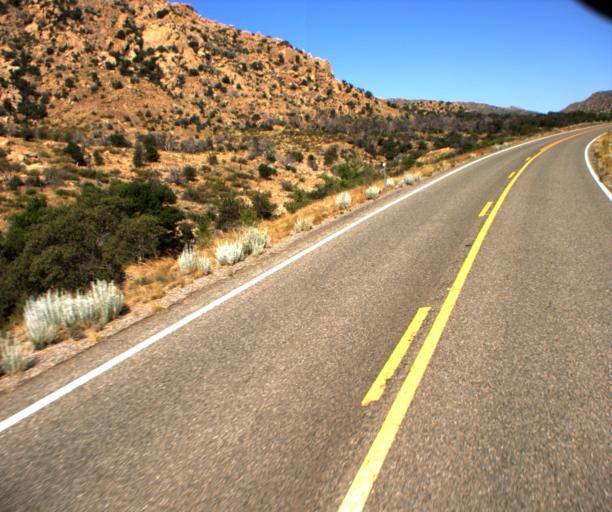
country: US
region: Arizona
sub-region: Graham County
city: Swift Trail Junction
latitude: 32.5634
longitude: -109.7997
